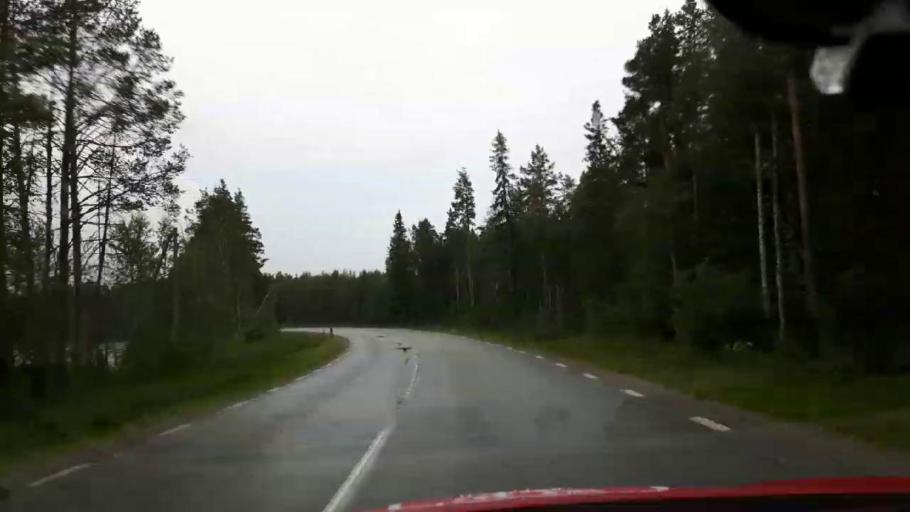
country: SE
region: Jaemtland
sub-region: OEstersunds Kommun
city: Brunflo
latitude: 62.8138
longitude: 14.9924
